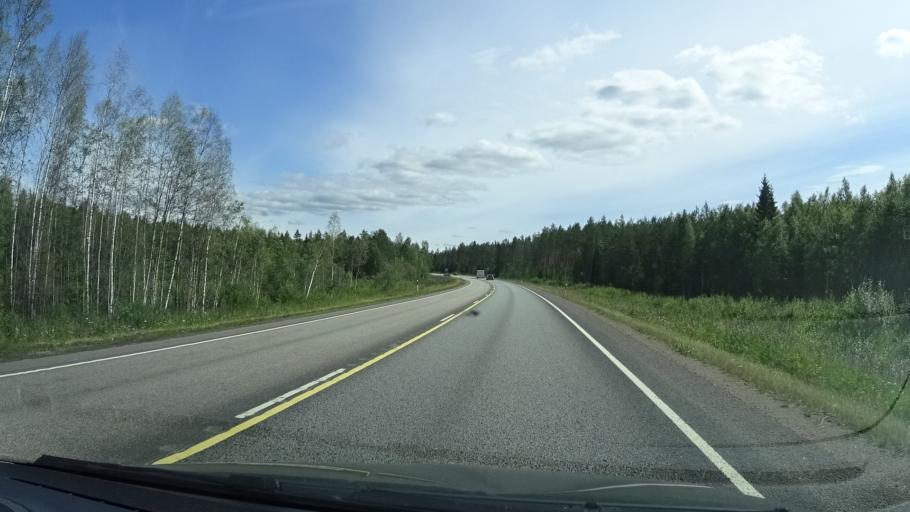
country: FI
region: Central Finland
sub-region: Jyvaeskylae
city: Uurainen
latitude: 62.2645
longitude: 25.4698
